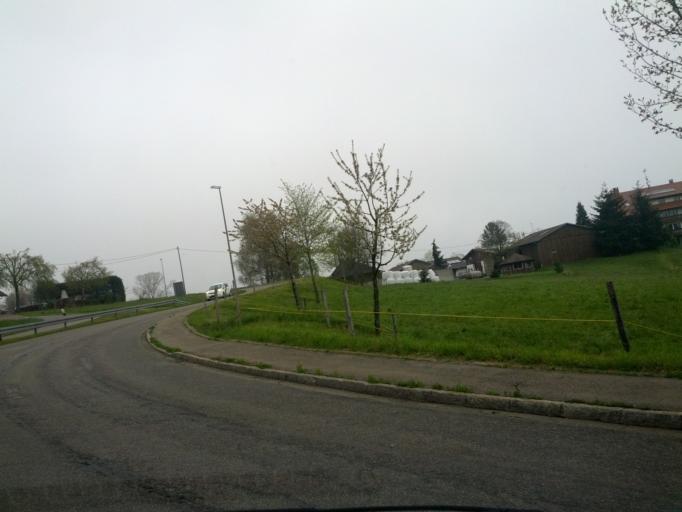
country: DE
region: Baden-Wuerttemberg
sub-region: Freiburg Region
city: Murg
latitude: 47.5962
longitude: 8.0264
